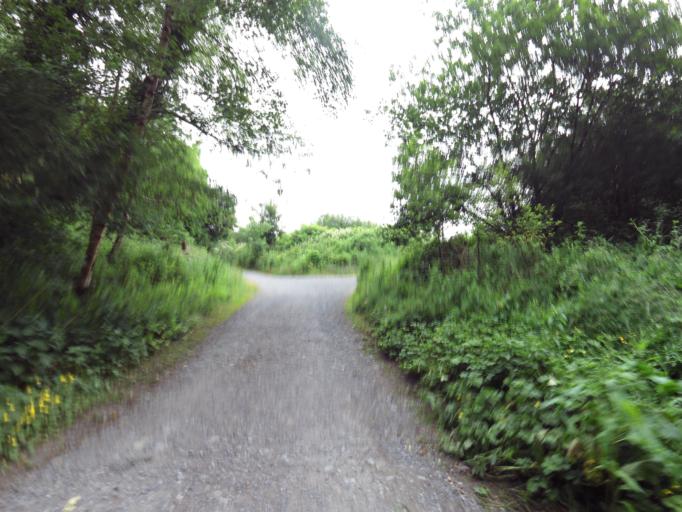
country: IE
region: Connaught
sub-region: County Galway
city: Gaillimh
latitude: 53.2935
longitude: -9.0787
